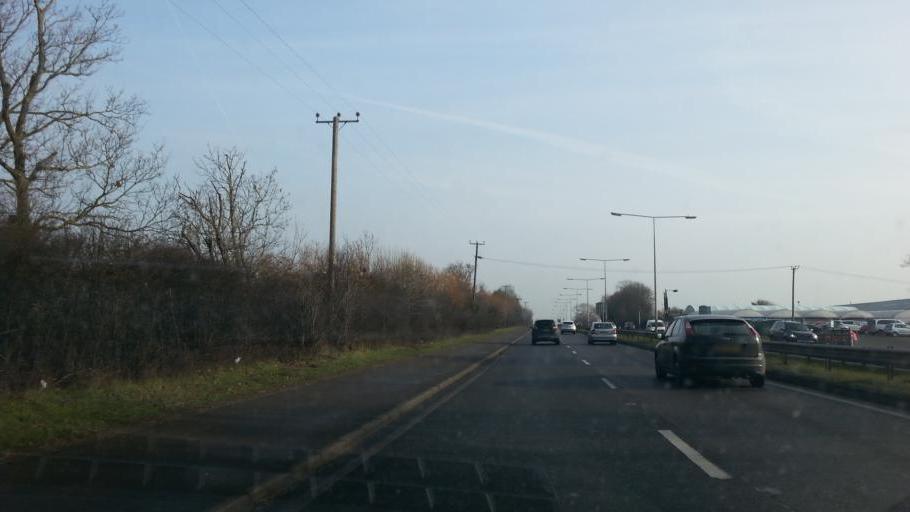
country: GB
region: England
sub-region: Essex
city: Wickford
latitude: 51.5898
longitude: 0.5379
